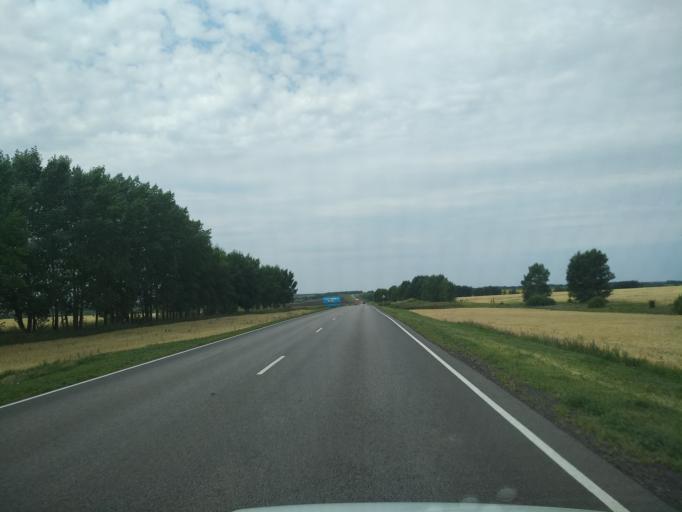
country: RU
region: Voronezj
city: Pereleshinskiy
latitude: 51.8615
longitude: 40.3577
